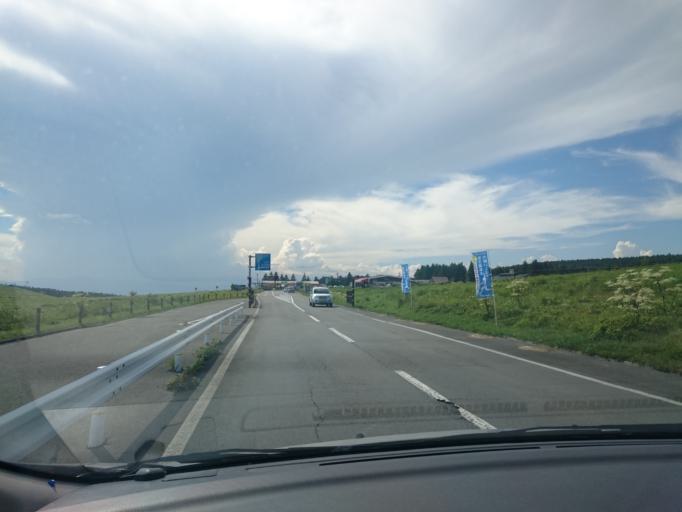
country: JP
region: Nagano
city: Suwa
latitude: 36.0966
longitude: 138.1707
